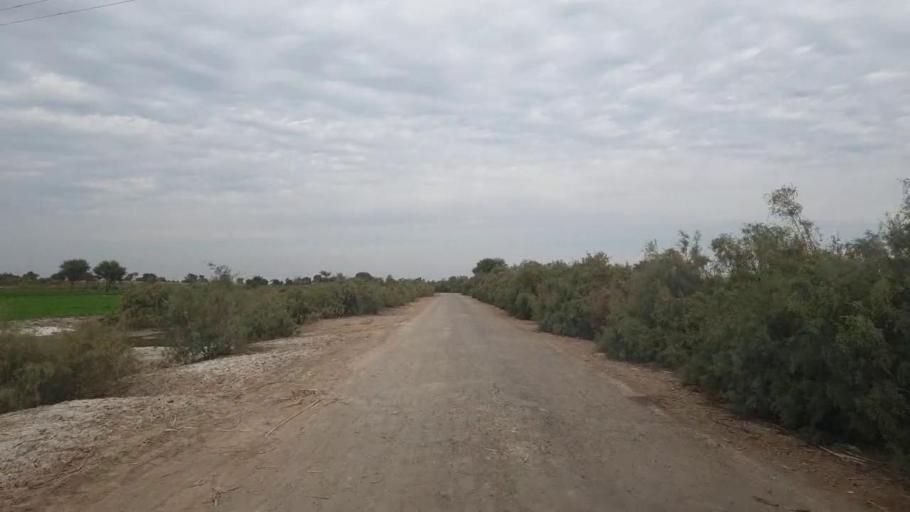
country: PK
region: Sindh
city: Jhol
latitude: 25.9992
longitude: 68.8811
